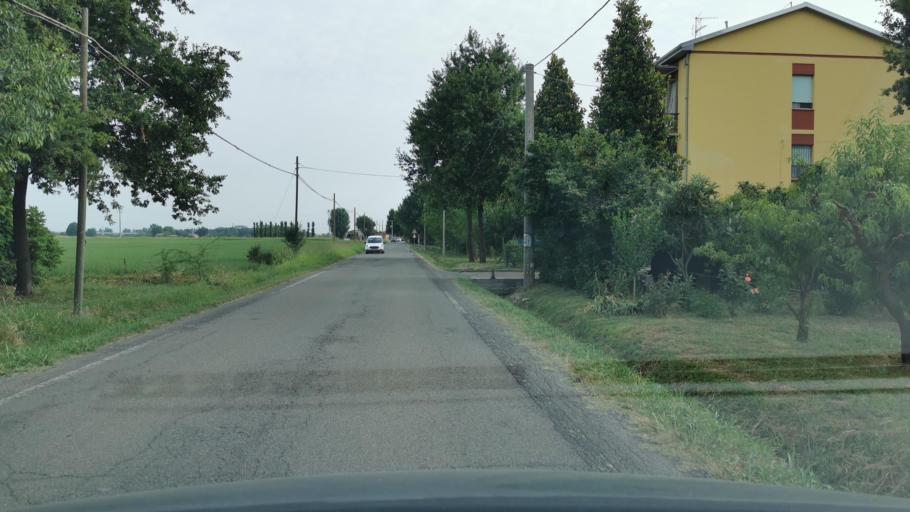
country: IT
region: Emilia-Romagna
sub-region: Provincia di Modena
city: Villanova
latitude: 44.6830
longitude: 10.9075
